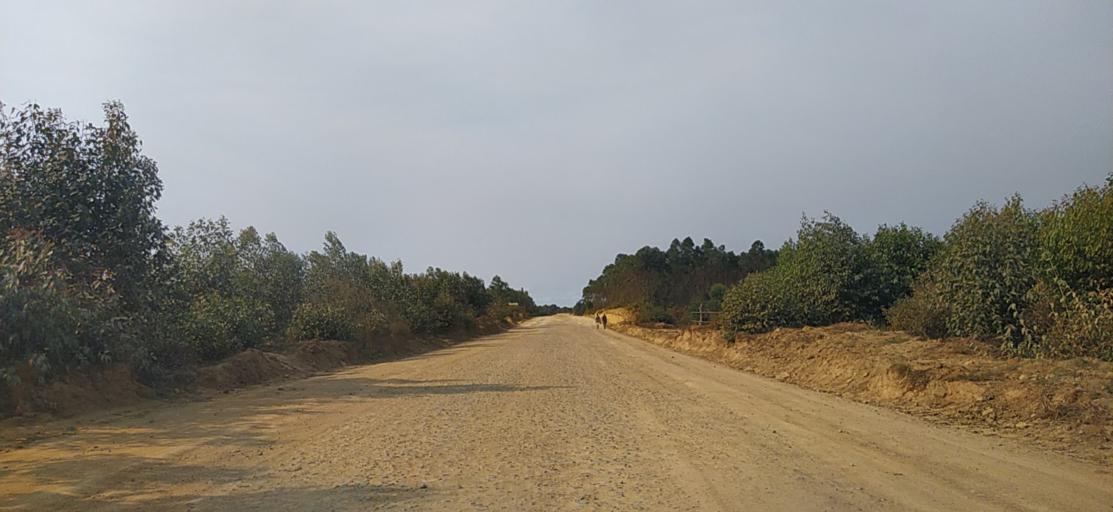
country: MG
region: Alaotra Mangoro
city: Moramanga
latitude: -18.6623
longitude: 48.2737
